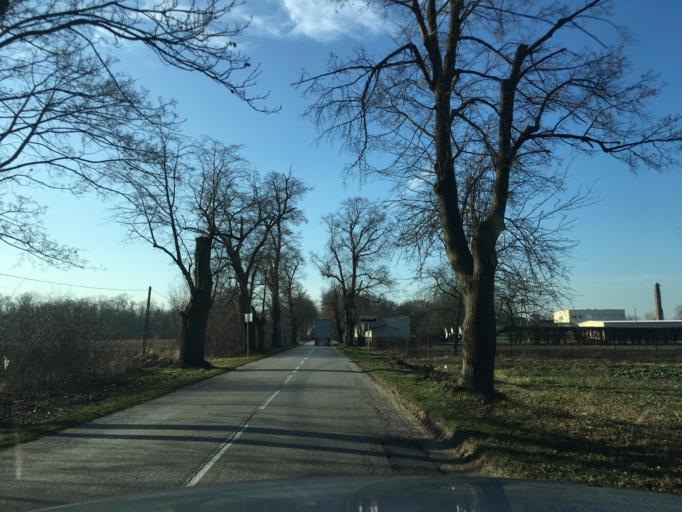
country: PL
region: Masovian Voivodeship
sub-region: Powiat pruszkowski
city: Nadarzyn
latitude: 52.0474
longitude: 20.7893
